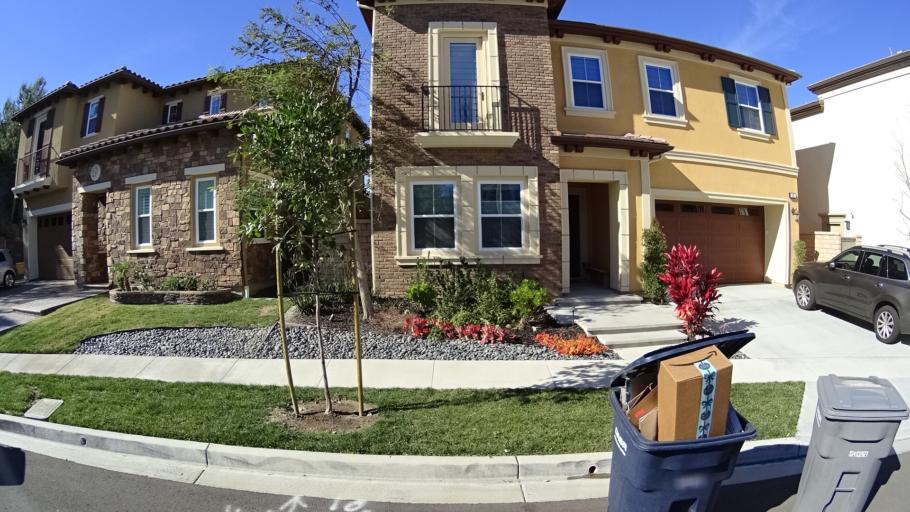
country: US
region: California
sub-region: Orange County
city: Lake Forest
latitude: 33.6698
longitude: -117.6842
